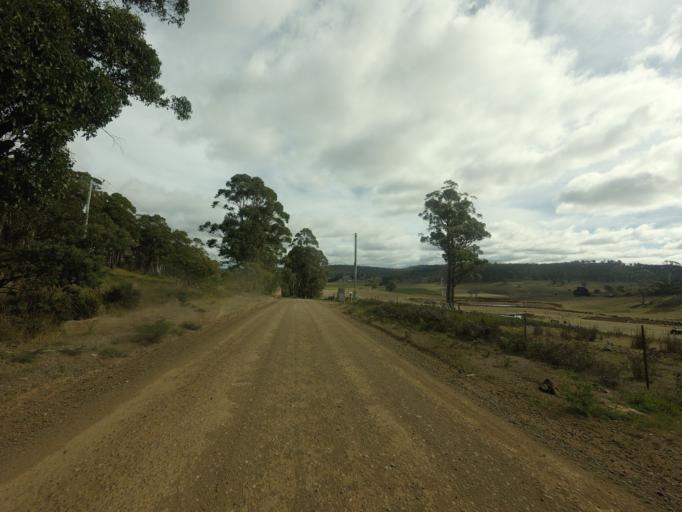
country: AU
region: Tasmania
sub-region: Brighton
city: Bridgewater
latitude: -42.3866
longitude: 147.4071
